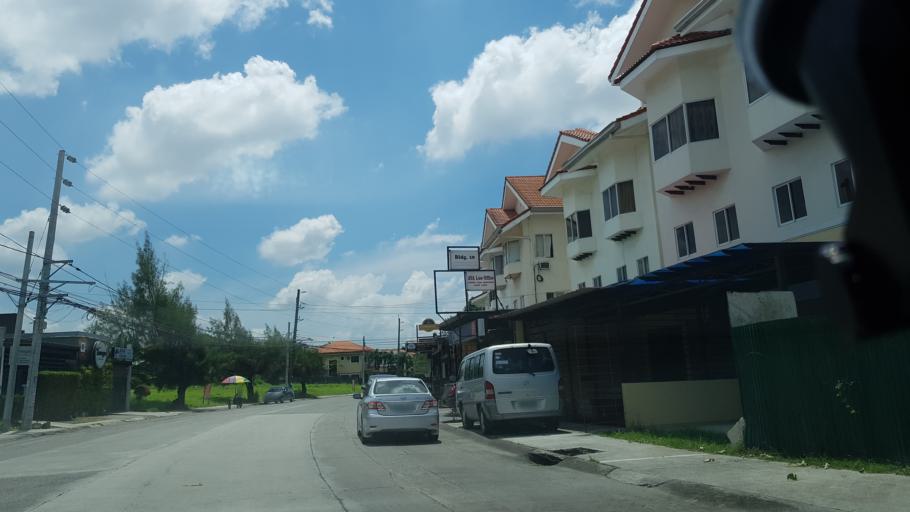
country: PH
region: Calabarzon
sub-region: Province of Rizal
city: Las Pinas
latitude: 14.4329
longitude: 120.9899
